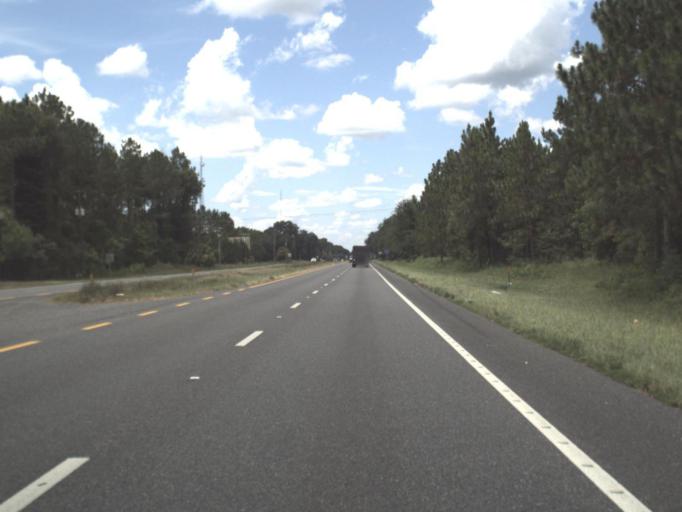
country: US
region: Florida
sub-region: Taylor County
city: Perry
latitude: 30.1393
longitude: -83.6060
